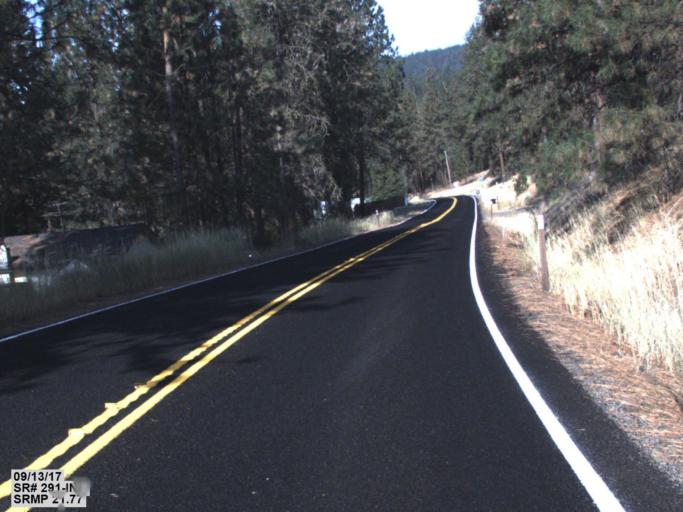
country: US
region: Washington
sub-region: Spokane County
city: Deer Park
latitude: 47.8913
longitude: -117.6751
